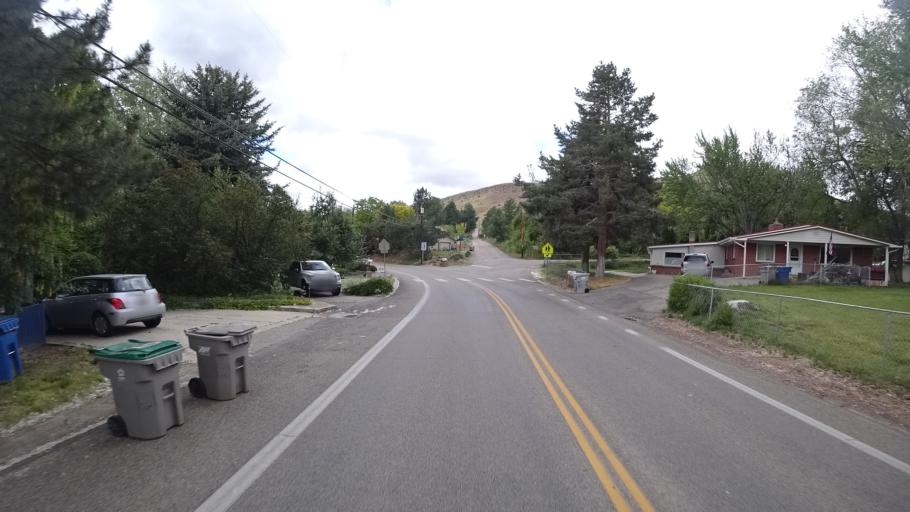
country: US
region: Idaho
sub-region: Ada County
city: Garden City
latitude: 43.6682
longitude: -116.2534
